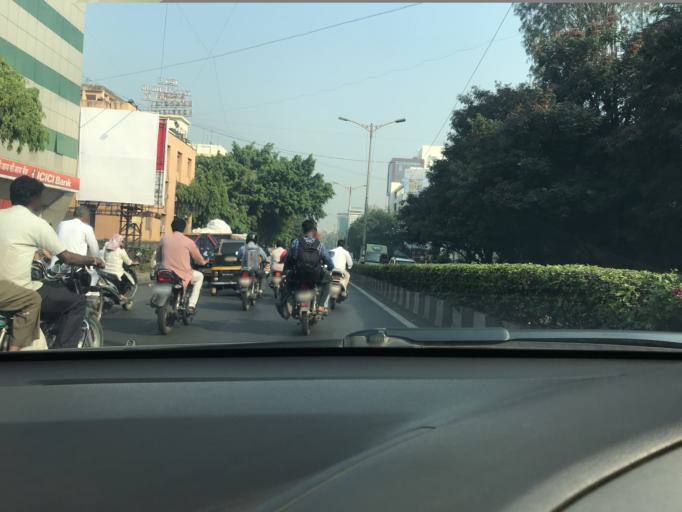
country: IN
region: Maharashtra
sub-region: Pune Division
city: Shivaji Nagar
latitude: 18.5266
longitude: 73.8298
